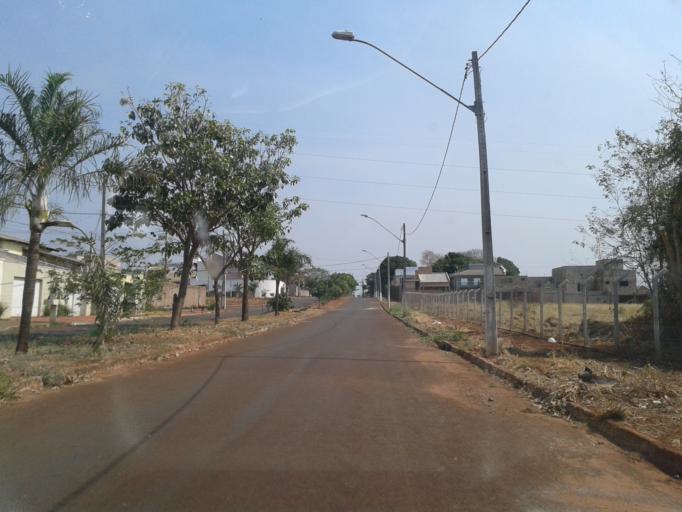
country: BR
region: Minas Gerais
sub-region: Ituiutaba
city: Ituiutaba
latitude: -18.9658
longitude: -49.4432
